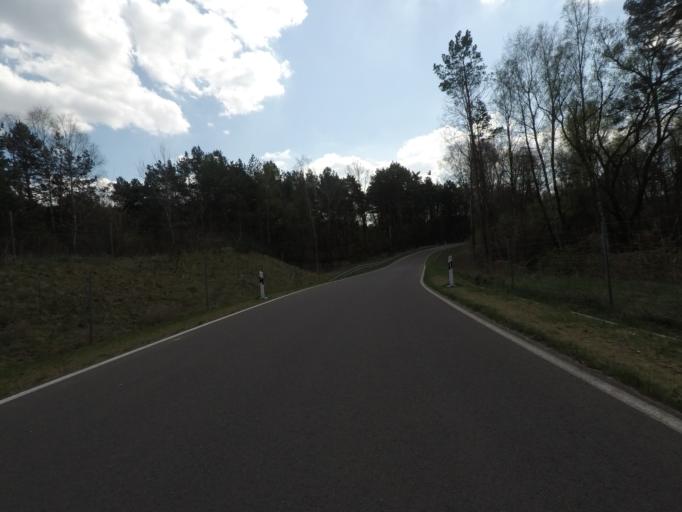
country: DE
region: Brandenburg
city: Melchow
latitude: 52.8366
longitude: 13.7025
